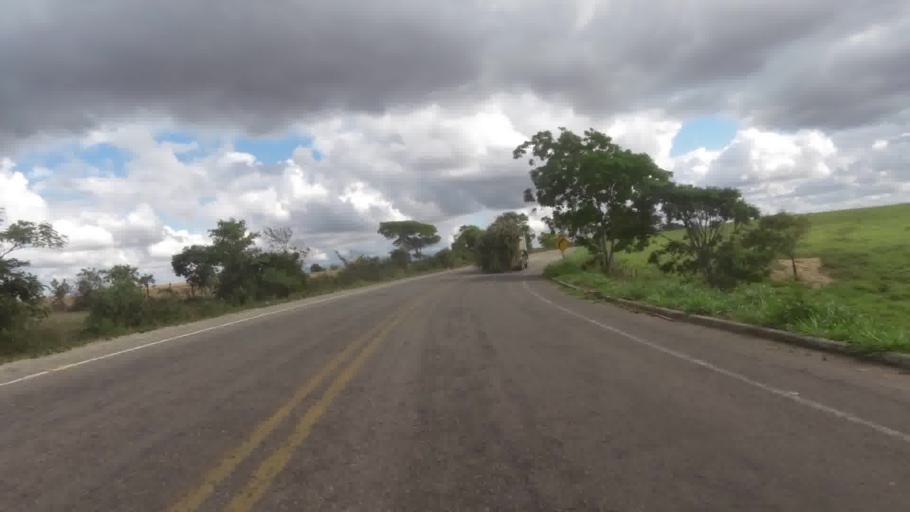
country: BR
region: Espirito Santo
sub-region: Marataizes
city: Marataizes
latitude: -21.1959
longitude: -40.9724
